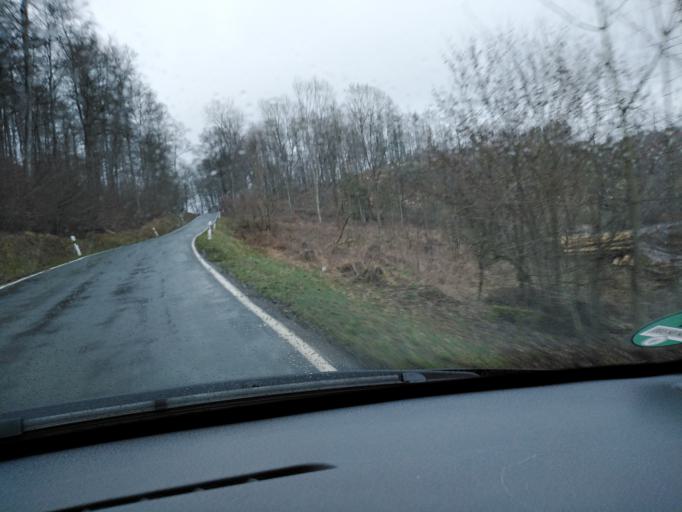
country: DE
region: North Rhine-Westphalia
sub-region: Regierungsbezirk Arnsberg
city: Brilon
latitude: 51.3825
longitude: 8.6343
